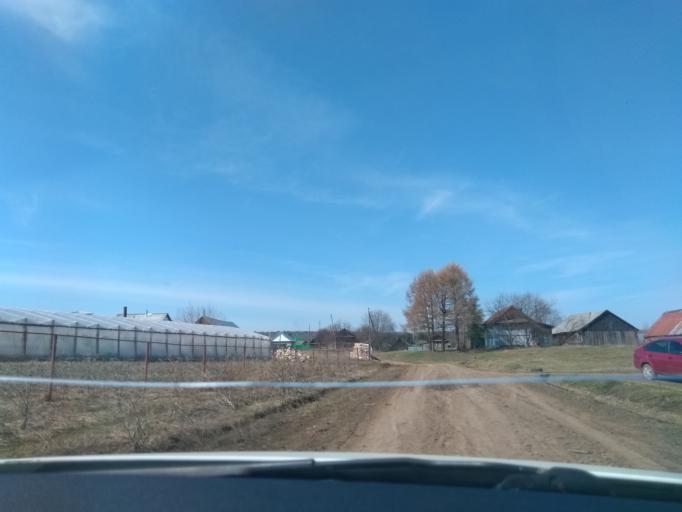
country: RU
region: Perm
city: Orda
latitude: 57.2181
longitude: 56.5983
